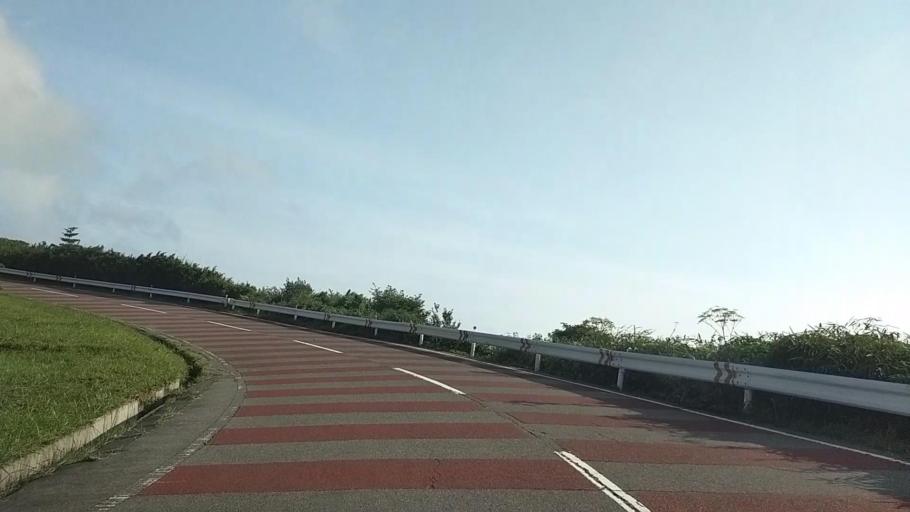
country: JP
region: Kanagawa
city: Hakone
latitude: 35.1975
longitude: 138.9920
